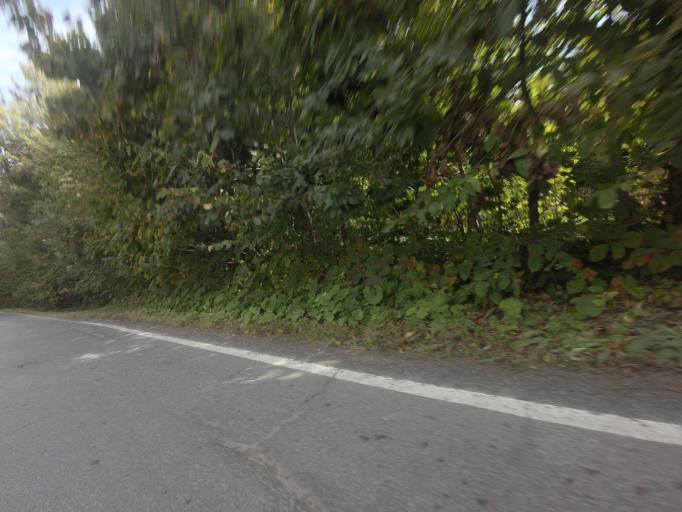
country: CA
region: Quebec
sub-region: Laurentides
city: Blainville
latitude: 45.6258
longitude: -73.9056
